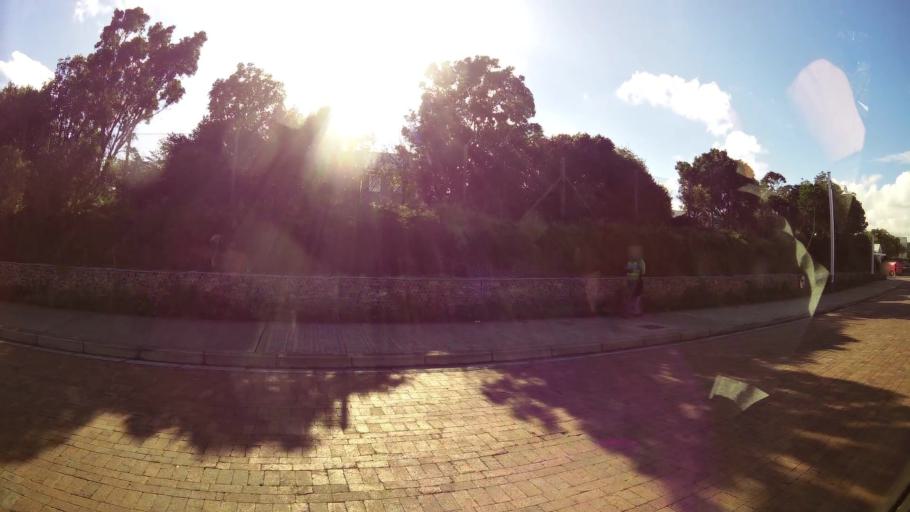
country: ZA
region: Western Cape
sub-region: Eden District Municipality
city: Knysna
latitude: -34.0463
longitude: 23.0481
